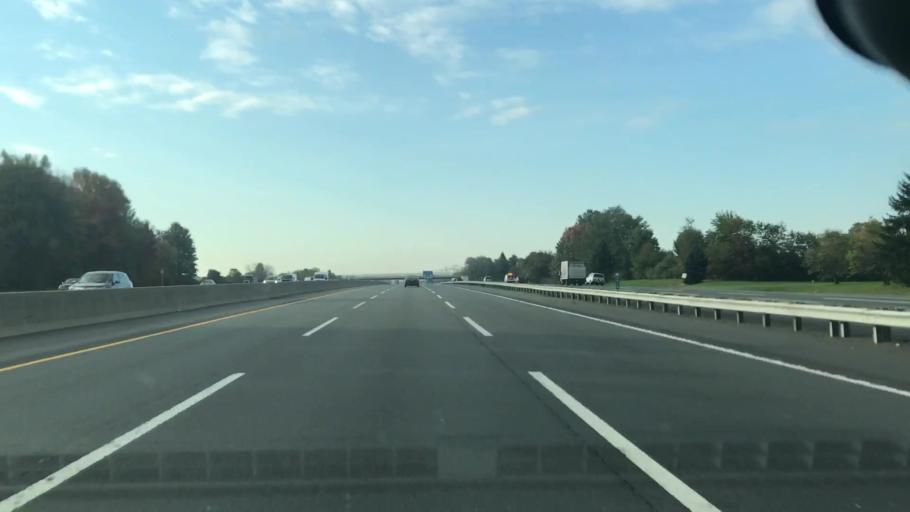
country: US
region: New Jersey
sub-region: Middlesex County
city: Helmetta
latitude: 40.4000
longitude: -74.4531
